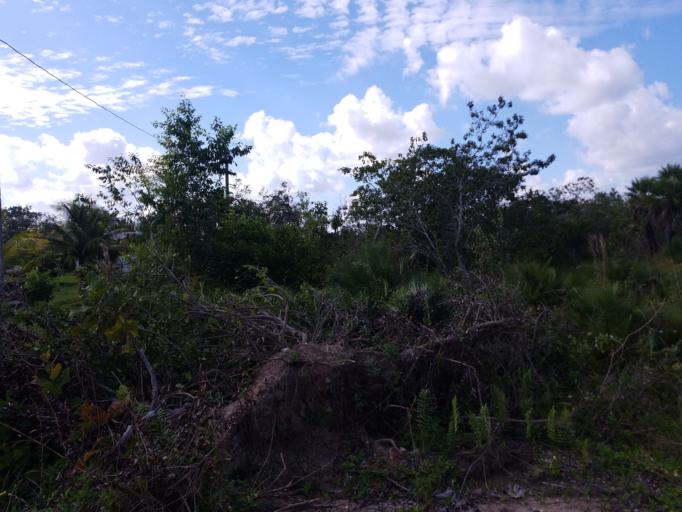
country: BZ
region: Belize
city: Belize City
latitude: 17.5656
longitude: -88.4115
